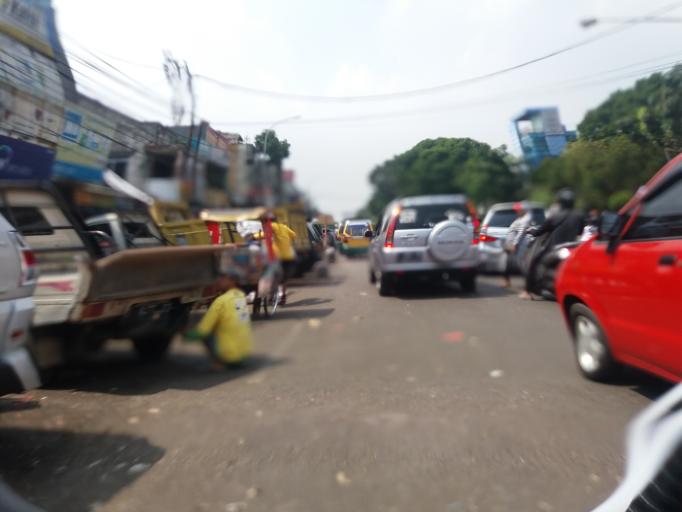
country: ID
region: West Java
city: Bandung
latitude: -6.9165
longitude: 107.5908
